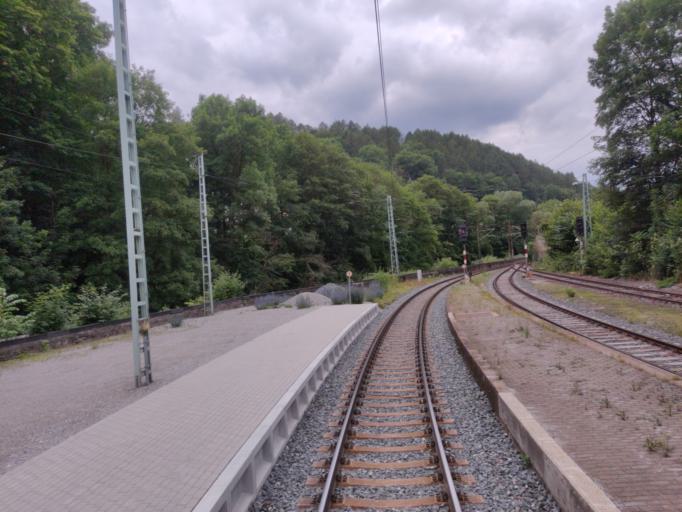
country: DE
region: Saxony-Anhalt
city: Rubeland
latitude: 51.7542
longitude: 10.8436
